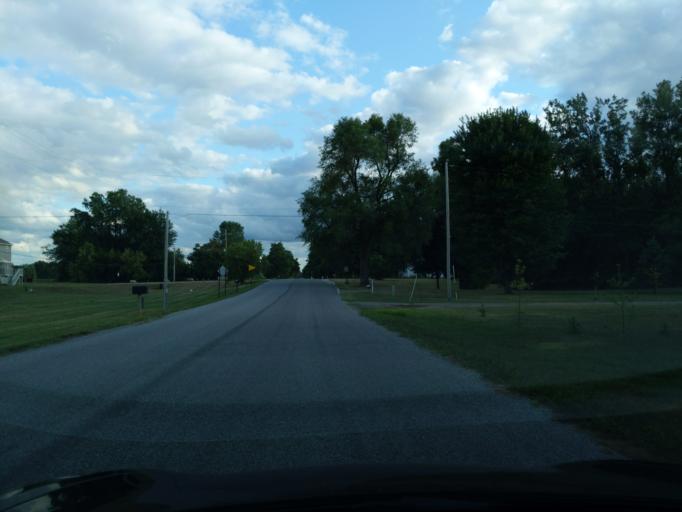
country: US
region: Michigan
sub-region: Ingham County
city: Holt
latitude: 42.6320
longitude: -84.5824
